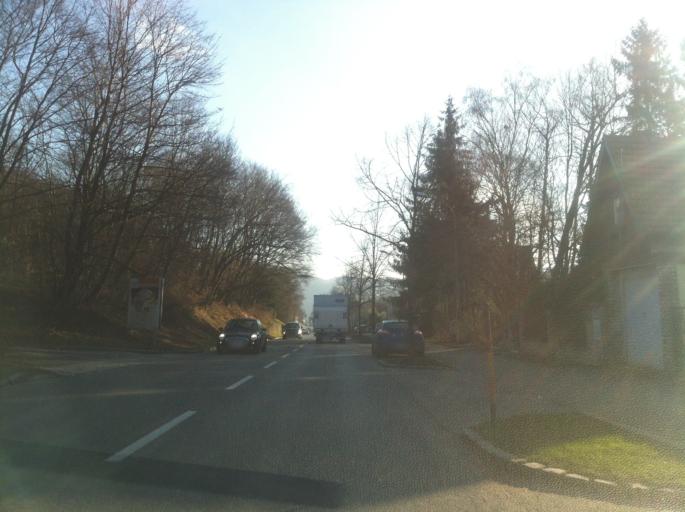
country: AT
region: Lower Austria
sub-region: Politischer Bezirk Wien-Umgebung
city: Gablitz
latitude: 48.2215
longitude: 16.1631
